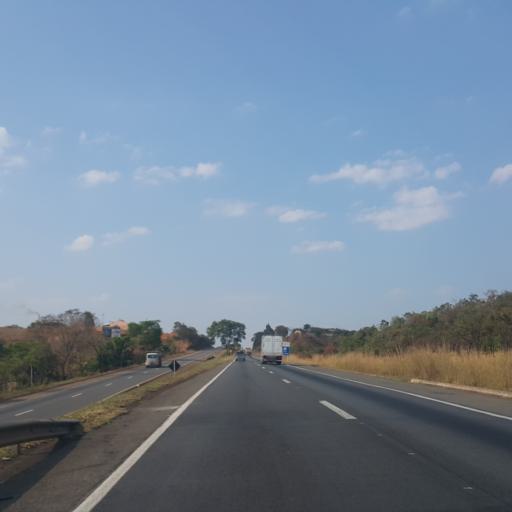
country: BR
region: Goias
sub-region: Abadiania
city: Abadiania
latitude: -16.0966
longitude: -48.5202
